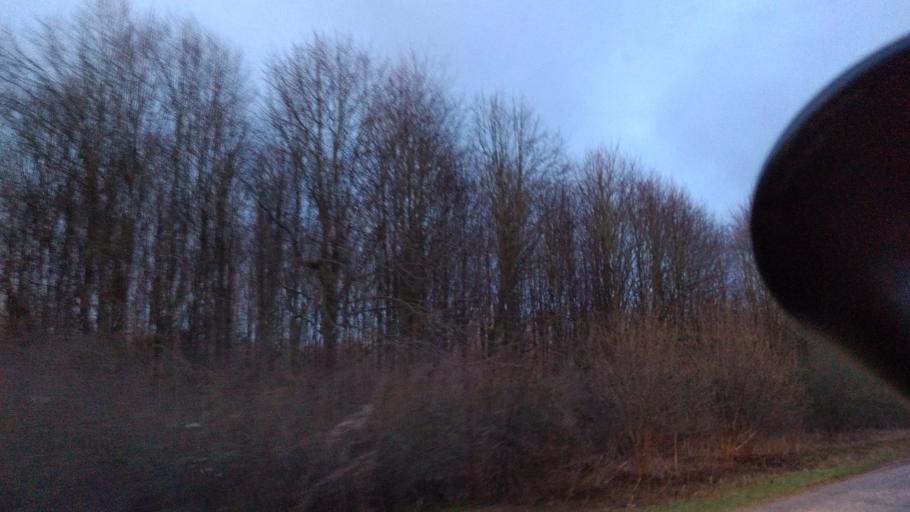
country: GB
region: England
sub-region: Borough of Swindon
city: Highworth
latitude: 51.5930
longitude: -1.7034
